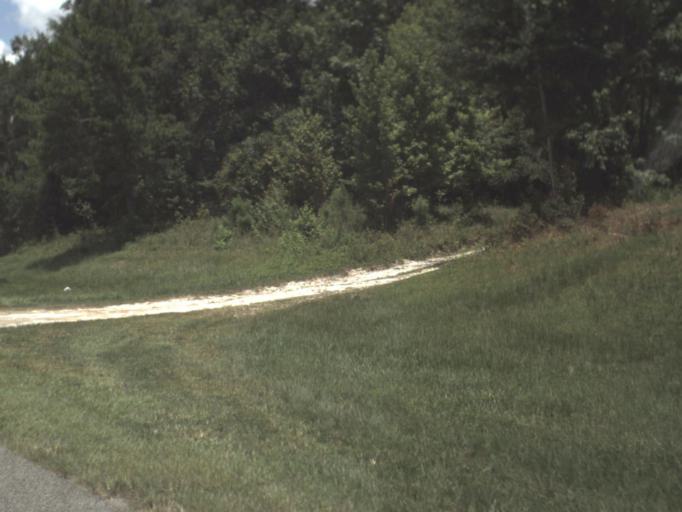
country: US
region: Florida
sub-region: Hernando County
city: North Brooksville
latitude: 28.5926
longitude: -82.4007
